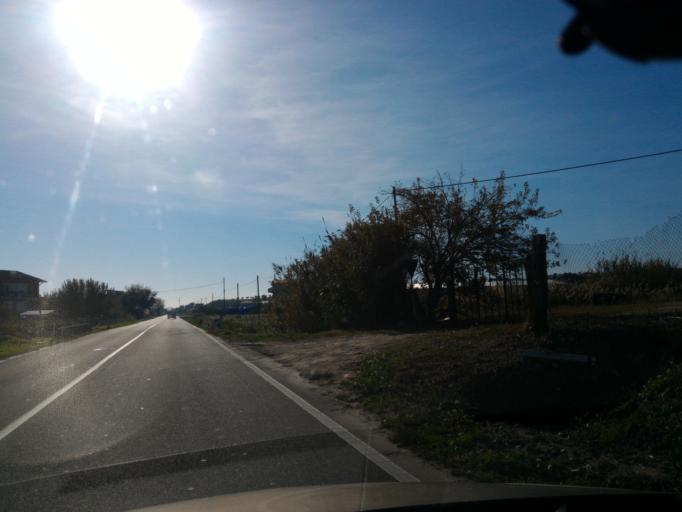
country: IT
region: Calabria
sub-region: Provincia di Crotone
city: Tronca
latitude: 39.2204
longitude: 17.1040
